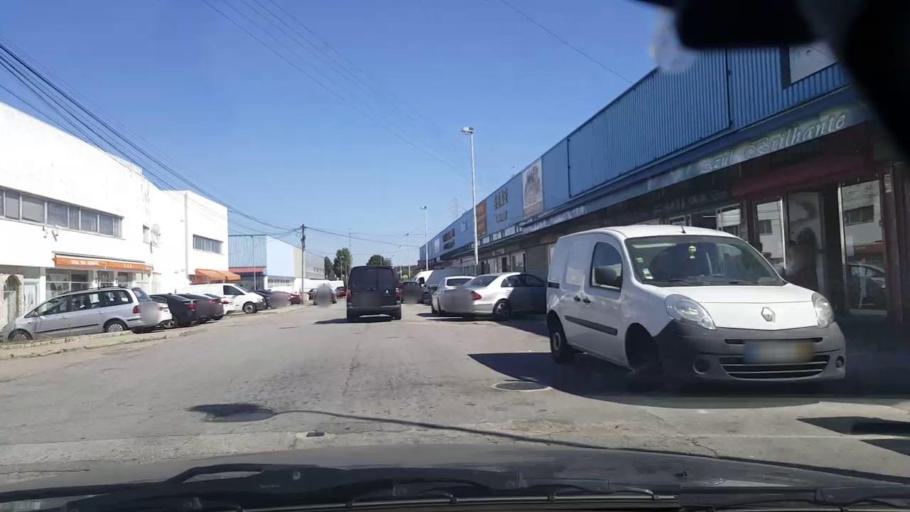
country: PT
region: Porto
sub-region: Vila do Conde
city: Arvore
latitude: 41.3241
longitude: -8.7121
